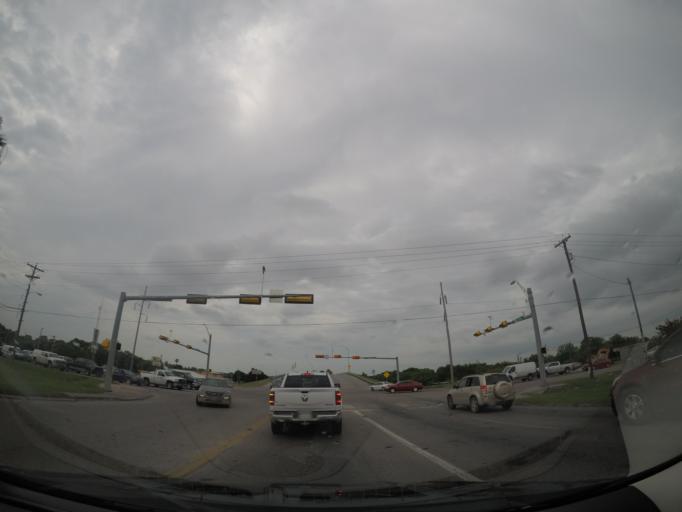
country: US
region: Texas
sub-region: Val Verde County
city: Del Rio
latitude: 29.3693
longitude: -100.8877
